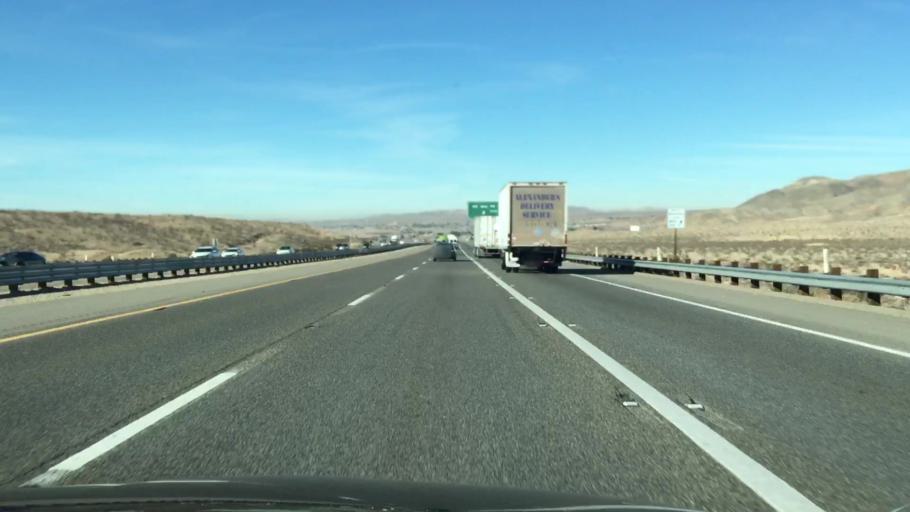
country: US
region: California
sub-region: San Bernardino County
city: Barstow
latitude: 34.9077
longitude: -116.9635
